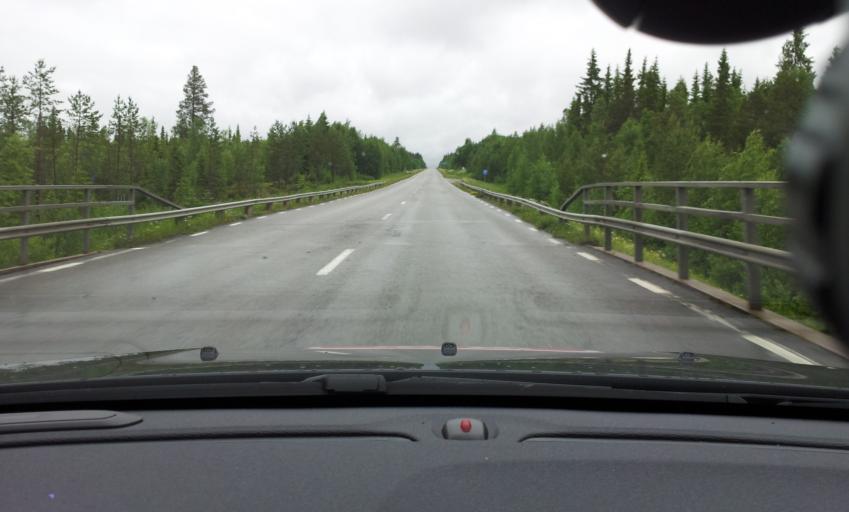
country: SE
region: Jaemtland
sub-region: Krokoms Kommun
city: Krokom
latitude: 63.4154
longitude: 14.4923
